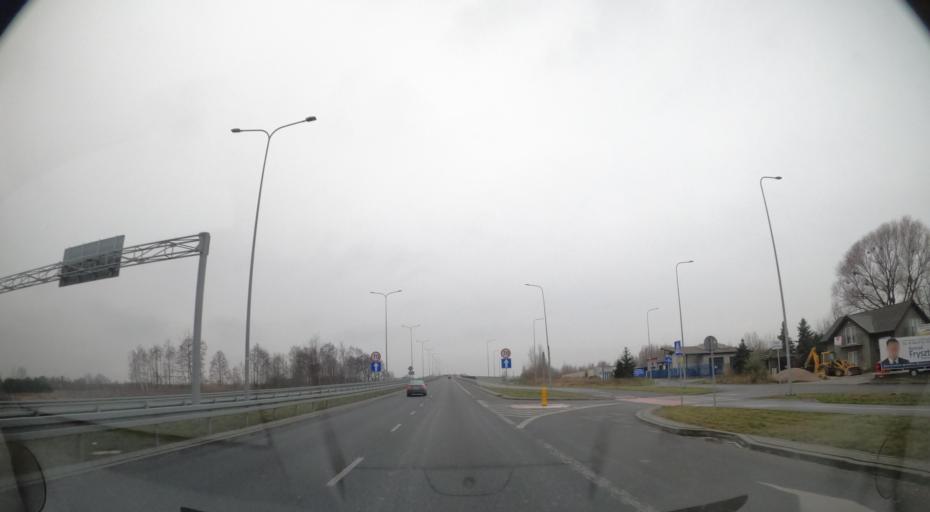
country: PL
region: Masovian Voivodeship
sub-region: Radom
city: Radom
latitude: 51.4122
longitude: 21.2033
